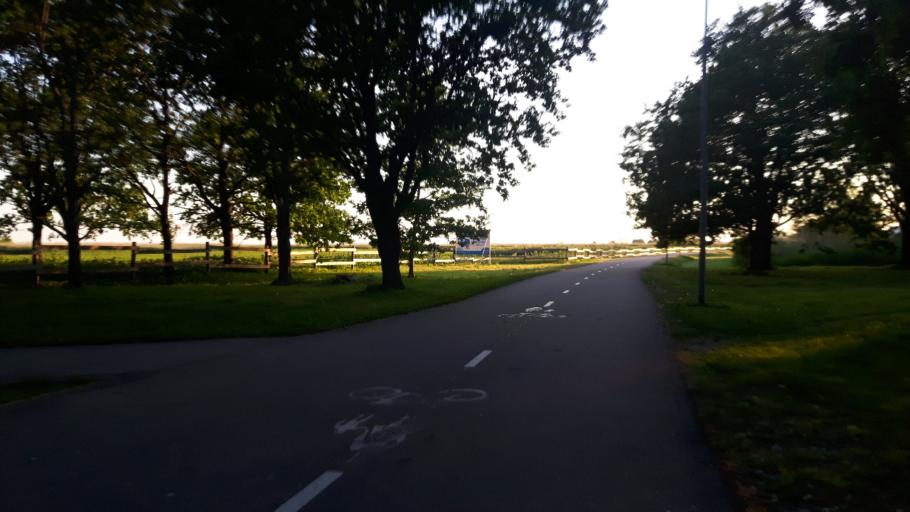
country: EE
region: Paernumaa
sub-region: Paernu linn
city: Parnu
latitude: 58.3704
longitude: 24.5255
